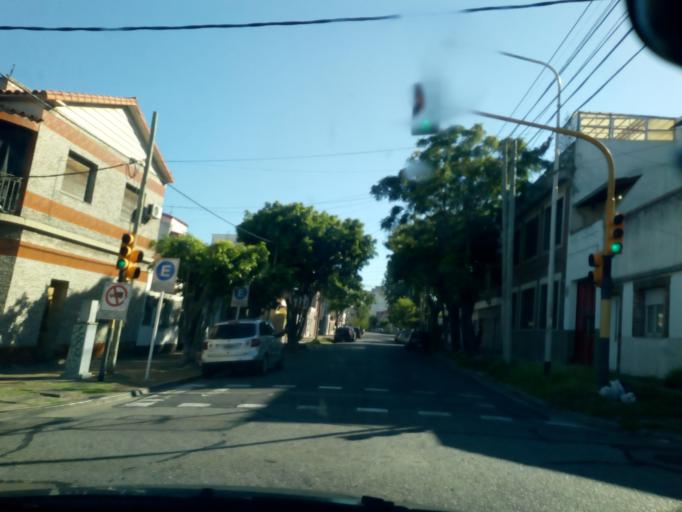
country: AR
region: Buenos Aires
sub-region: Partido de Avellaneda
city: Avellaneda
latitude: -34.6723
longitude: -58.3592
